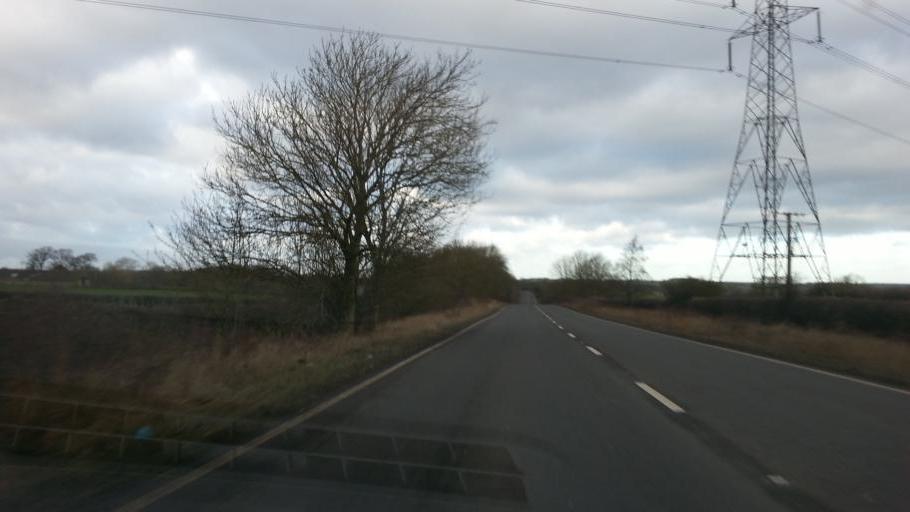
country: GB
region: England
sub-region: Nottinghamshire
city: Farndon
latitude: 53.1220
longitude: -0.8740
